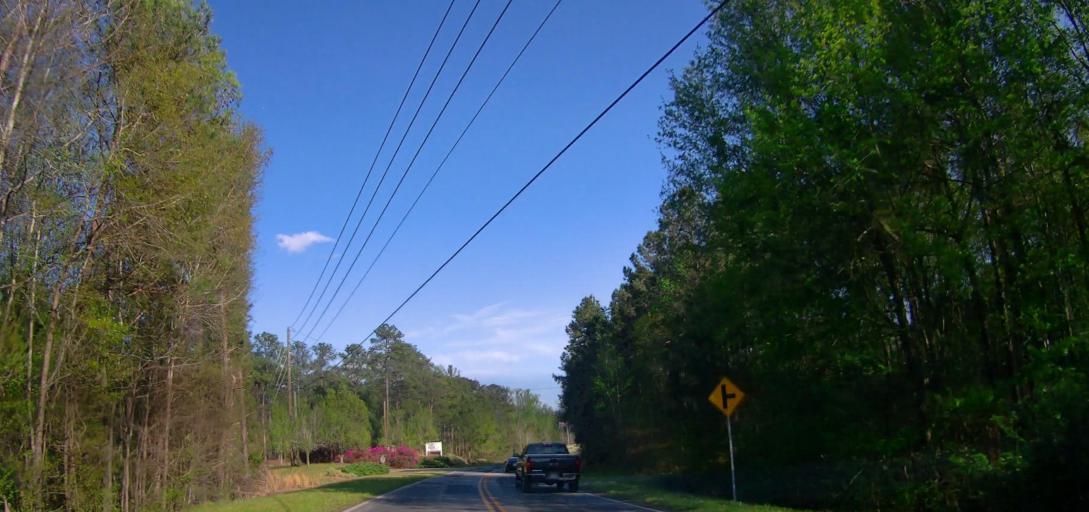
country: US
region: Georgia
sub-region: Baldwin County
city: Milledgeville
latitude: 33.1390
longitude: -83.2400
